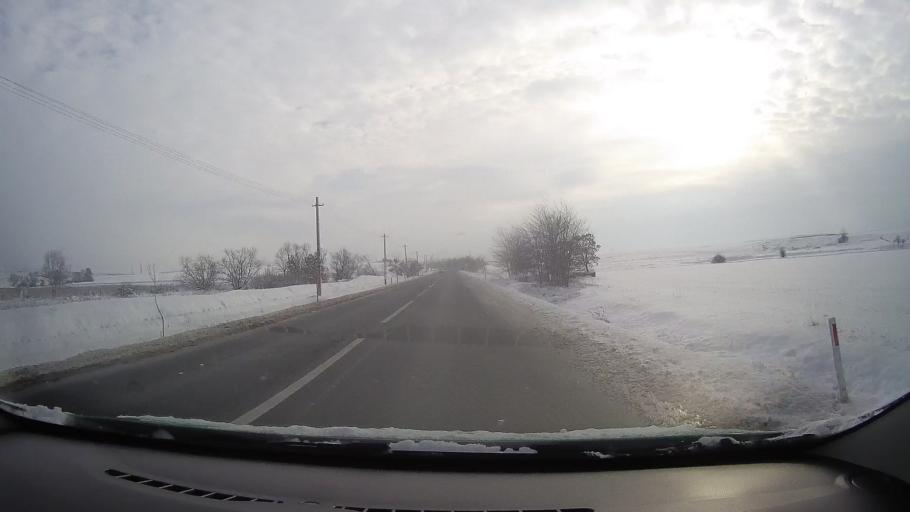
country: RO
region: Alba
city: Vurpar
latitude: 45.9869
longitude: 23.5090
